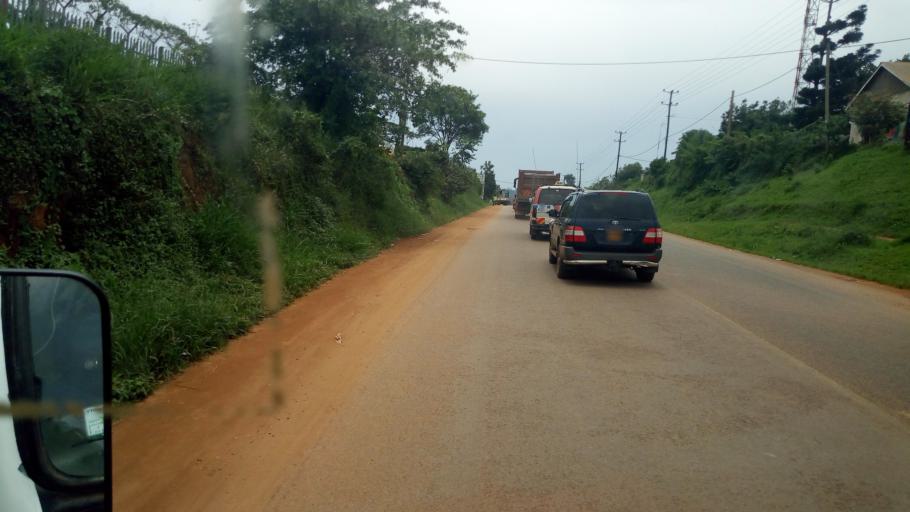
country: UG
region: Central Region
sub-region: Wakiso District
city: Kireka
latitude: 0.4163
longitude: 32.5964
